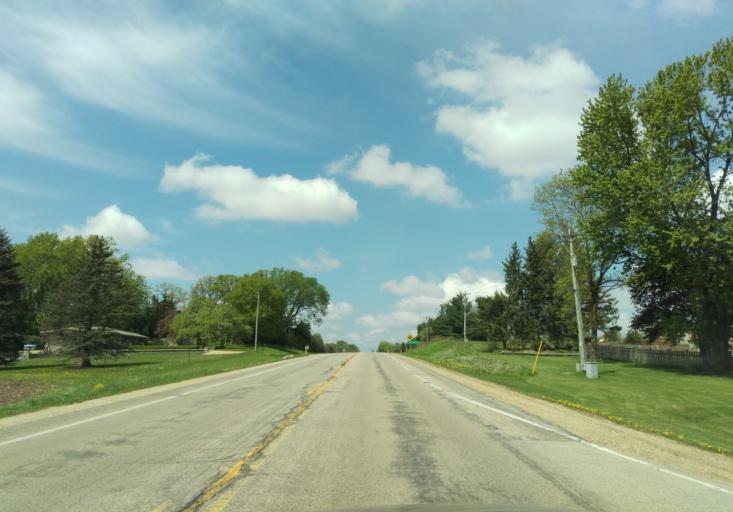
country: US
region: Wisconsin
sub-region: Dane County
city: Cross Plains
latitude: 43.0602
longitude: -89.5878
